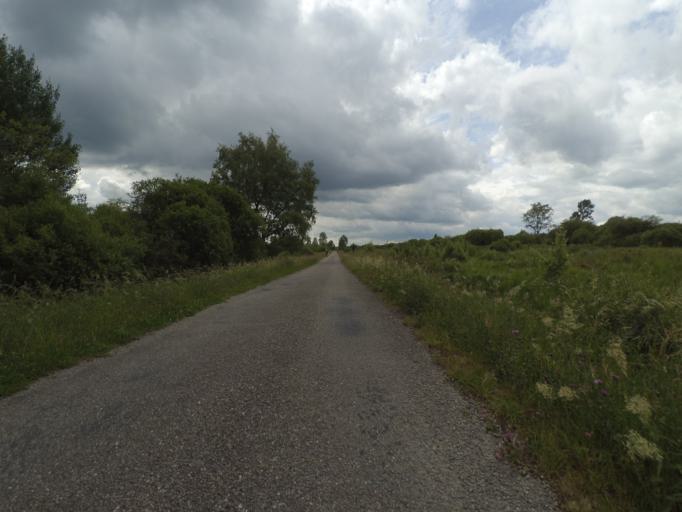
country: DE
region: North Rhine-Westphalia
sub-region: Regierungsbezirk Koln
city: Monschau
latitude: 50.5774
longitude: 6.1804
